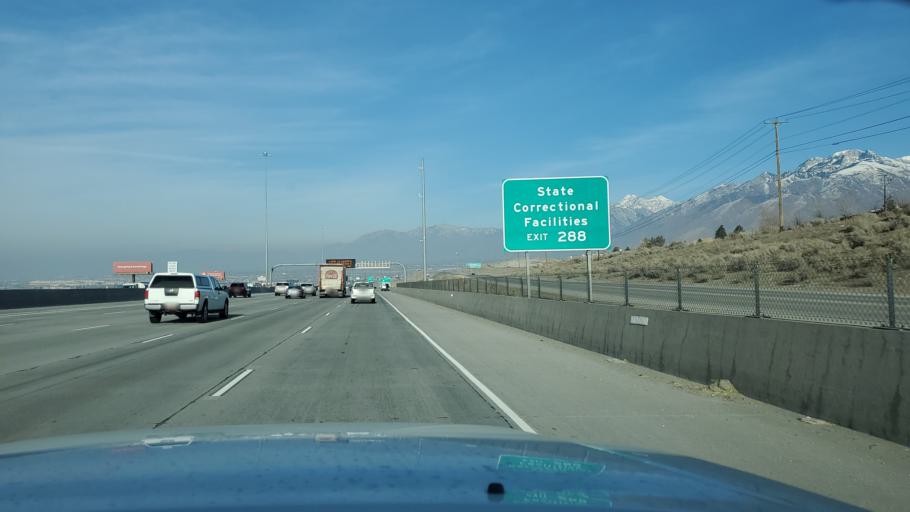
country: US
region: Utah
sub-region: Salt Lake County
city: Bluffdale
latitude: 40.4695
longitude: -111.9084
